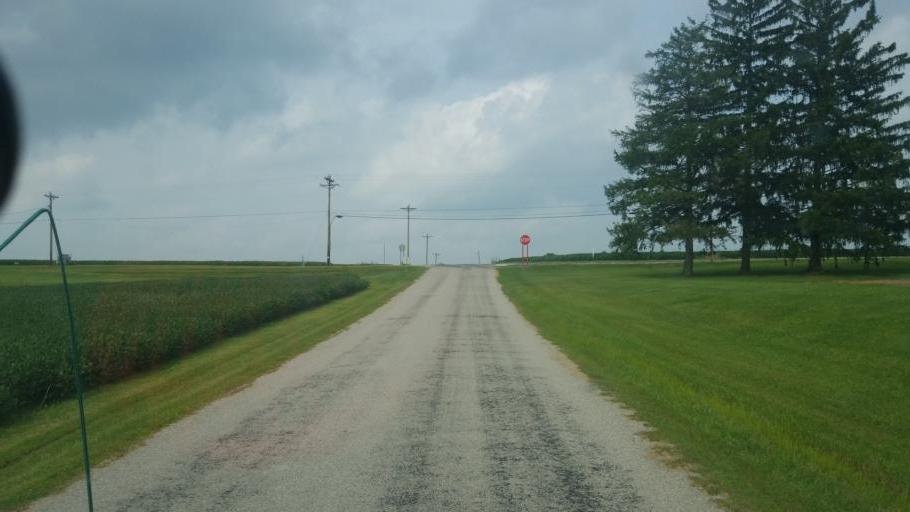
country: US
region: Ohio
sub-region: Huron County
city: New London
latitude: 41.0895
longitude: -82.4622
